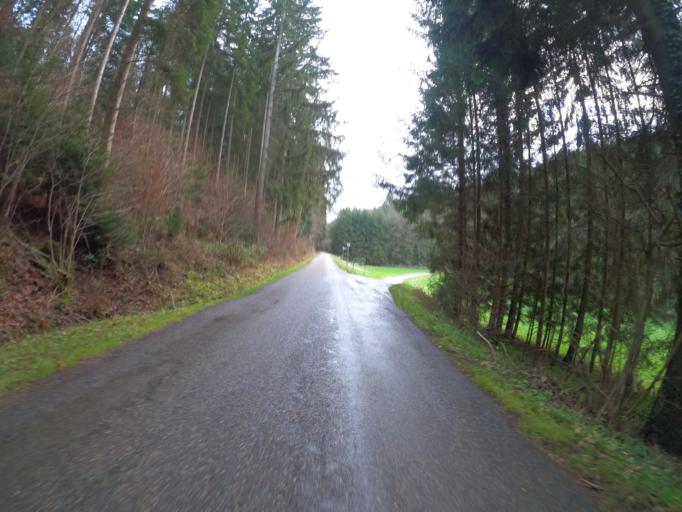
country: DE
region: Baden-Wuerttemberg
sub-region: Regierungsbezirk Stuttgart
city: Lorch
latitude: 48.7864
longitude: 9.7233
